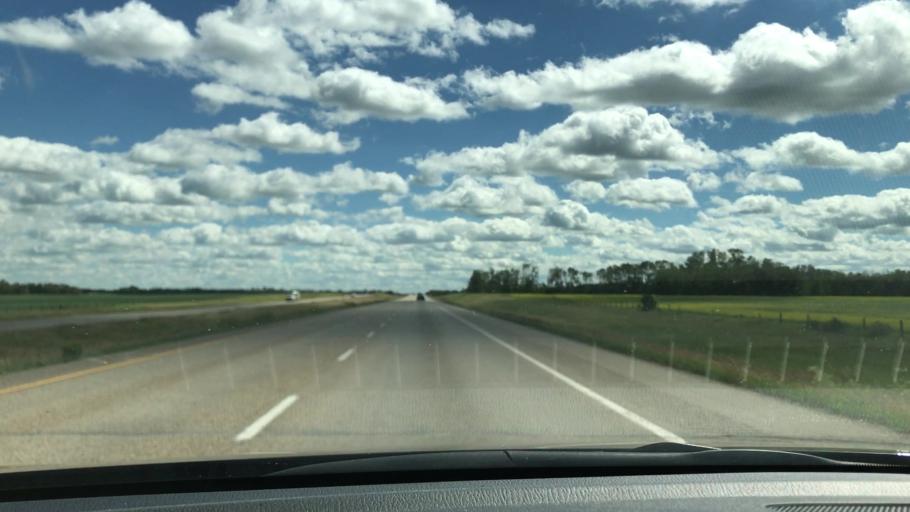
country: CA
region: Alberta
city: Millet
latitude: 53.1306
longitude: -113.5983
